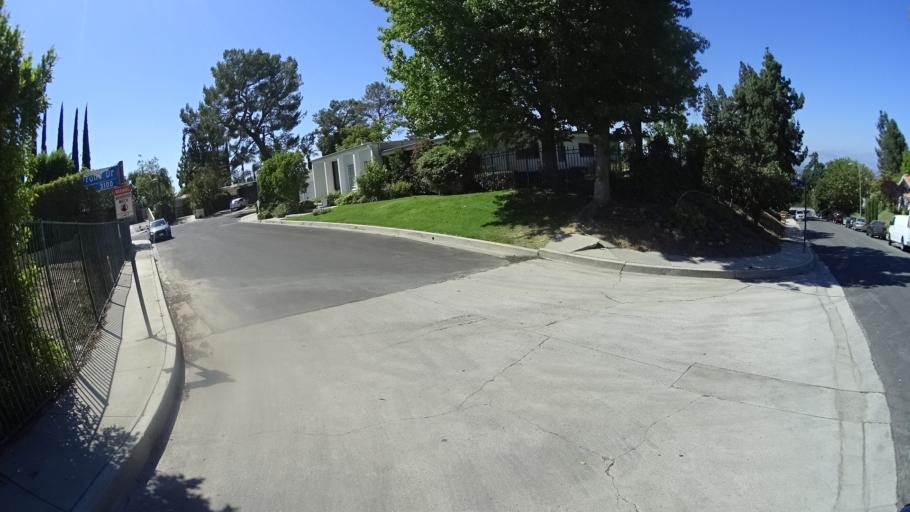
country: US
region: California
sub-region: Los Angeles County
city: Sherman Oaks
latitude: 34.1327
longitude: -118.4839
